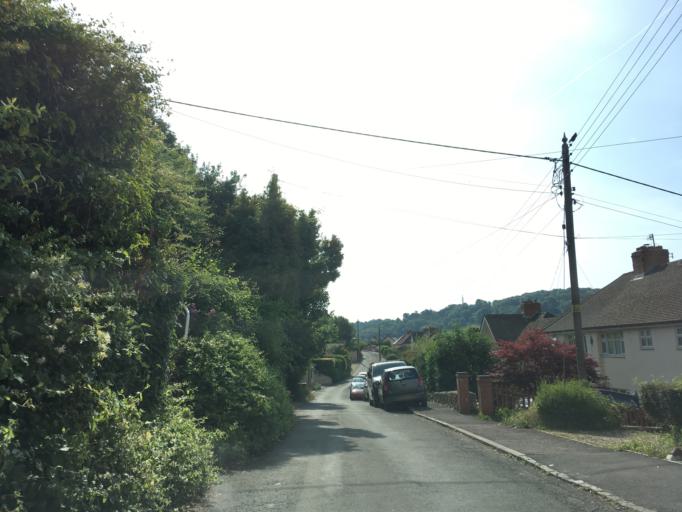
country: GB
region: England
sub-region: Gloucestershire
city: Brimscombe
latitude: 51.7204
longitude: -2.1878
